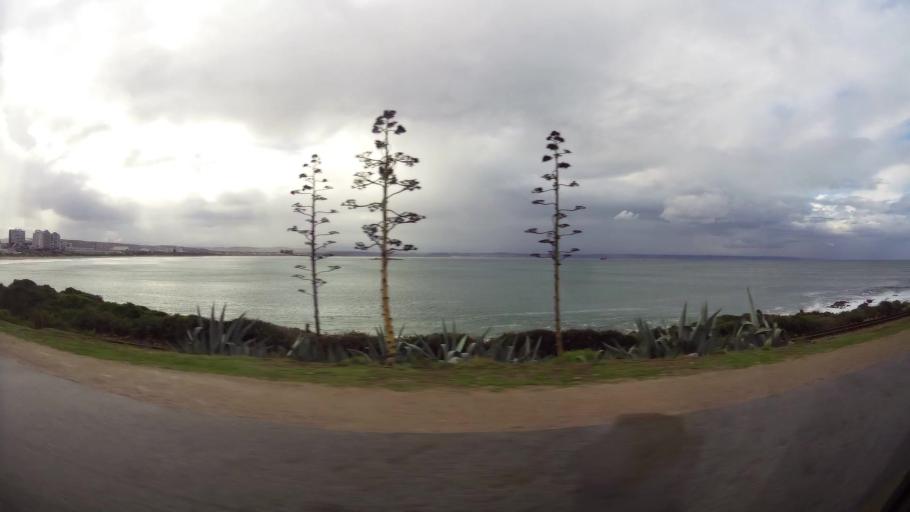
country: ZA
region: Western Cape
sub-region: Eden District Municipality
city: Mossel Bay
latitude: -34.1667
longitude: 22.1165
